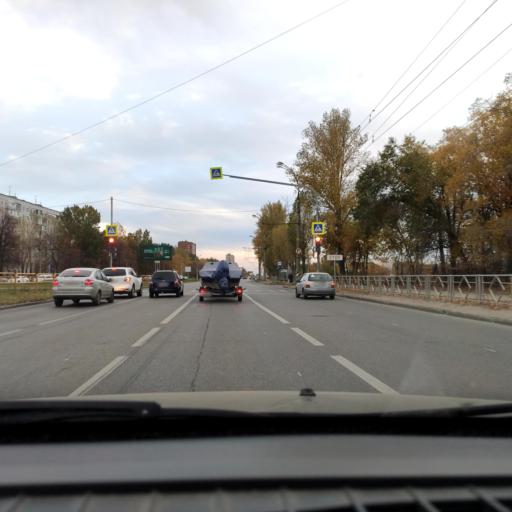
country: RU
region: Samara
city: Tol'yatti
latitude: 53.5194
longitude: 49.2584
